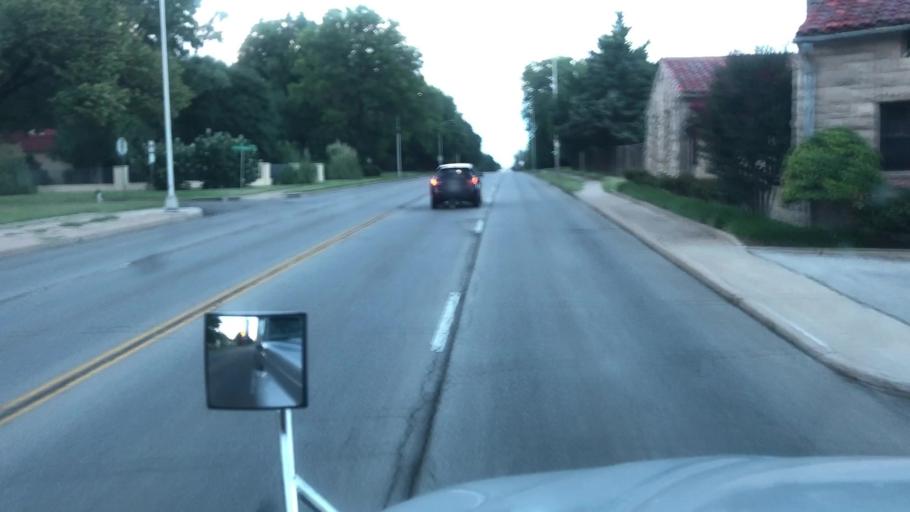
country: US
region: Oklahoma
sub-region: Kay County
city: Ponca City
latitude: 36.7138
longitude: -97.0672
